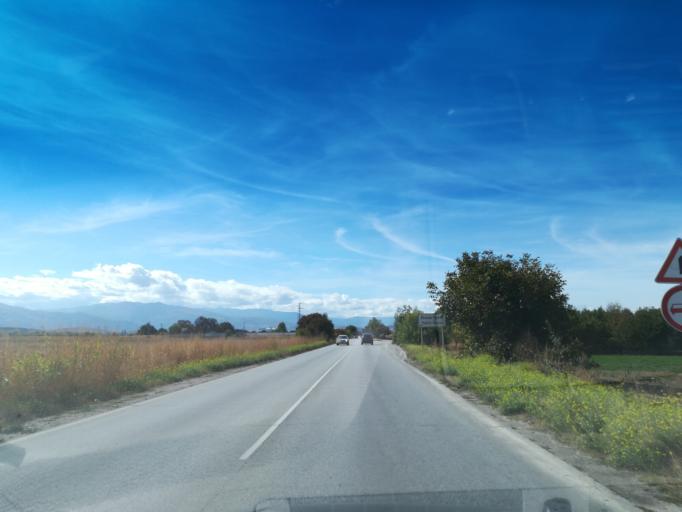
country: BG
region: Plovdiv
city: Stamboliyski
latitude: 42.1224
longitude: 24.5798
